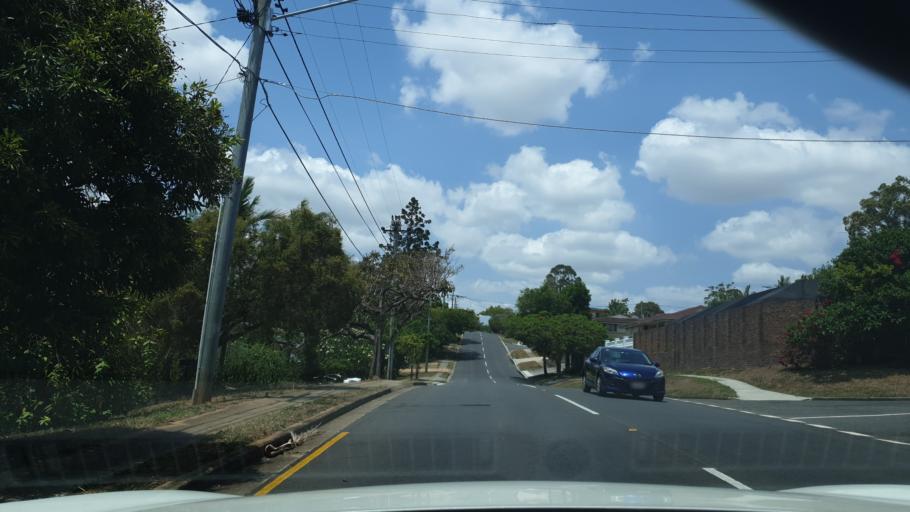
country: AU
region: Queensland
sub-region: Brisbane
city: Chermside West
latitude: -27.3697
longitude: 153.0256
